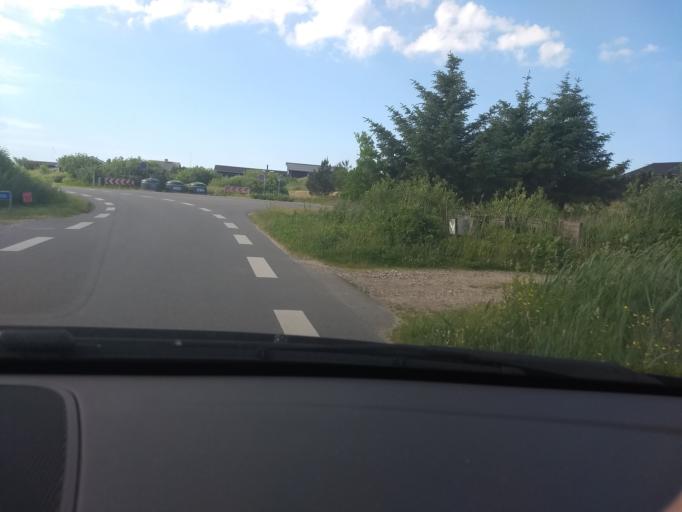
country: DE
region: Schleswig-Holstein
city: List
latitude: 55.1340
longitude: 8.4926
